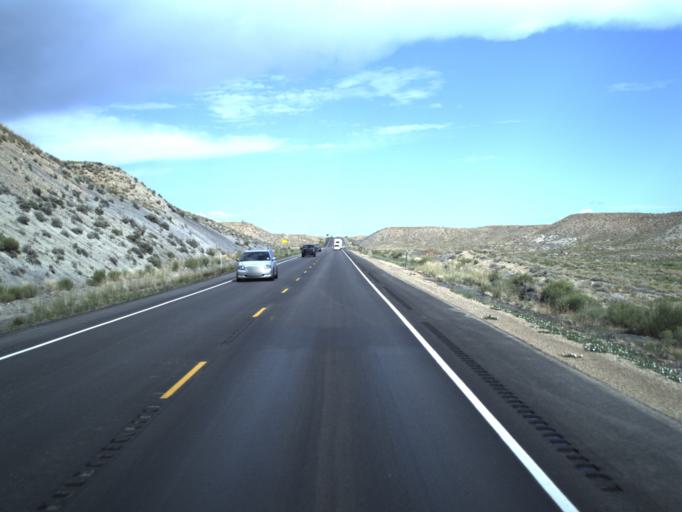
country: US
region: Utah
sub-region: Carbon County
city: East Carbon City
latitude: 39.4714
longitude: -110.4994
